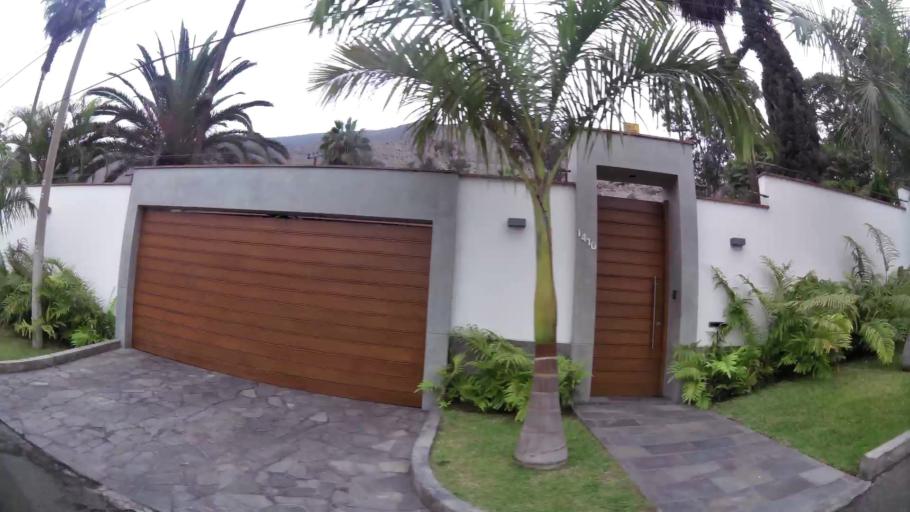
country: PE
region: Lima
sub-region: Lima
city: La Molina
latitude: -12.0911
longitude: -76.9228
